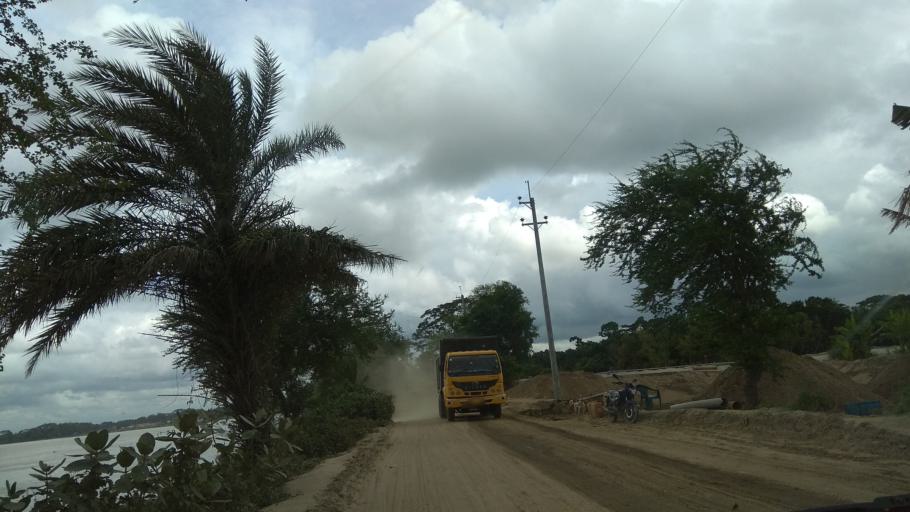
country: BD
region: Khulna
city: Kalia
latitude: 23.2029
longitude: 89.6980
